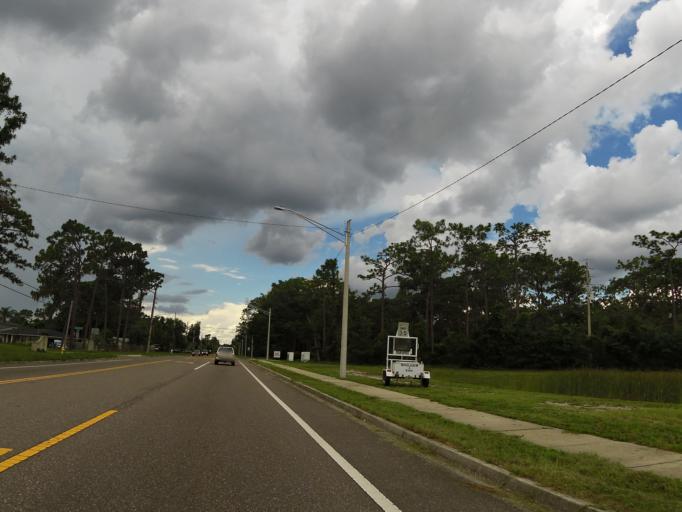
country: US
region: Florida
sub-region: Duval County
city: Jacksonville
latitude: 30.4165
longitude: -81.6652
